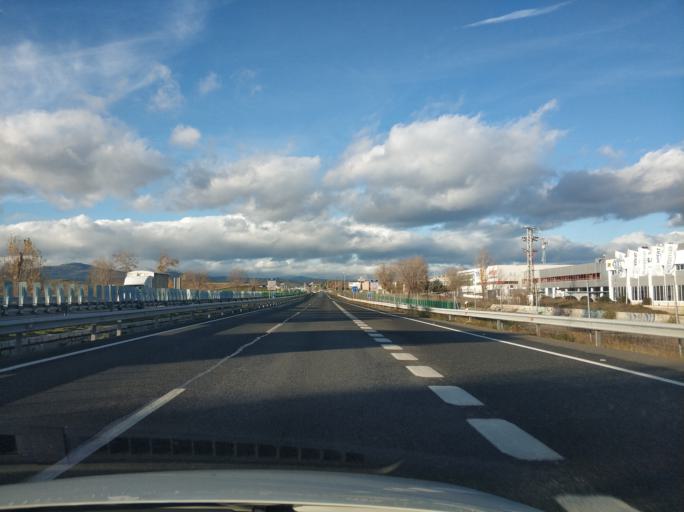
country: ES
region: Madrid
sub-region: Provincia de Madrid
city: San Agustin de Guadalix
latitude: 40.6495
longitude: -3.5970
